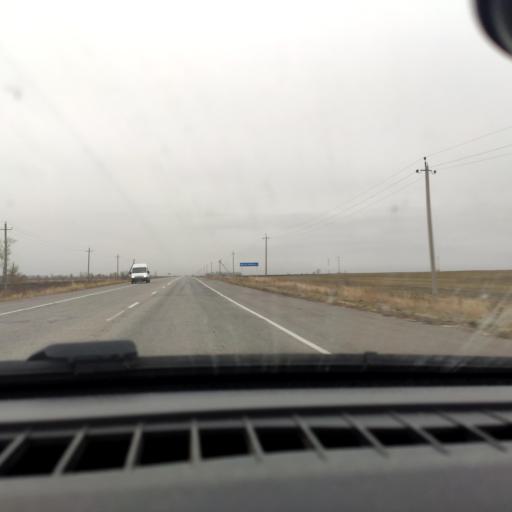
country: RU
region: Voronezj
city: Strelitsa
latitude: 51.5518
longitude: 38.9721
